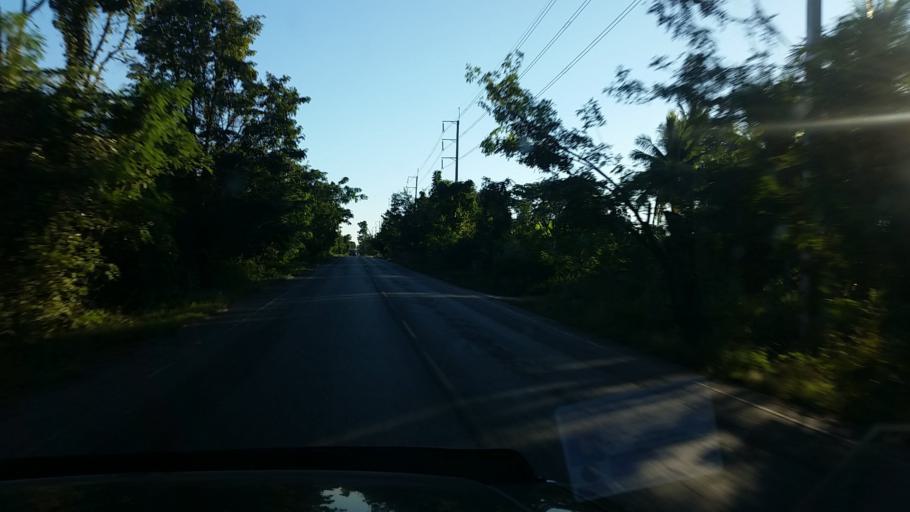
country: TH
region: Chaiyaphum
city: Nong Bua Rawe
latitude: 15.6995
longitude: 101.7354
